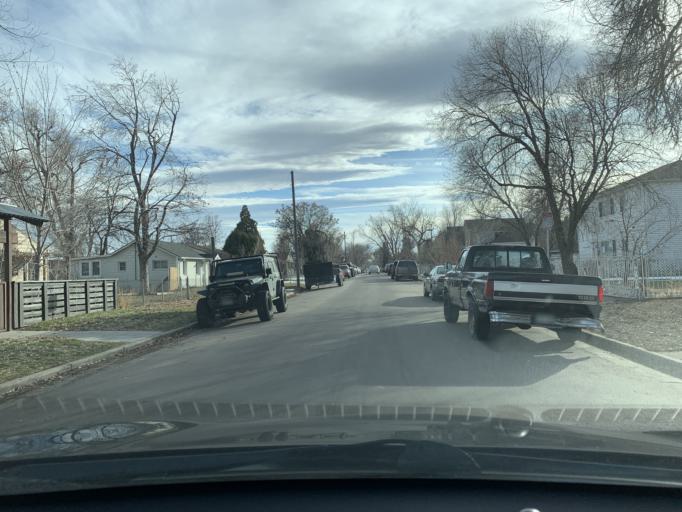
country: US
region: Colorado
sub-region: Denver County
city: Denver
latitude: 39.7347
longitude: -105.0264
